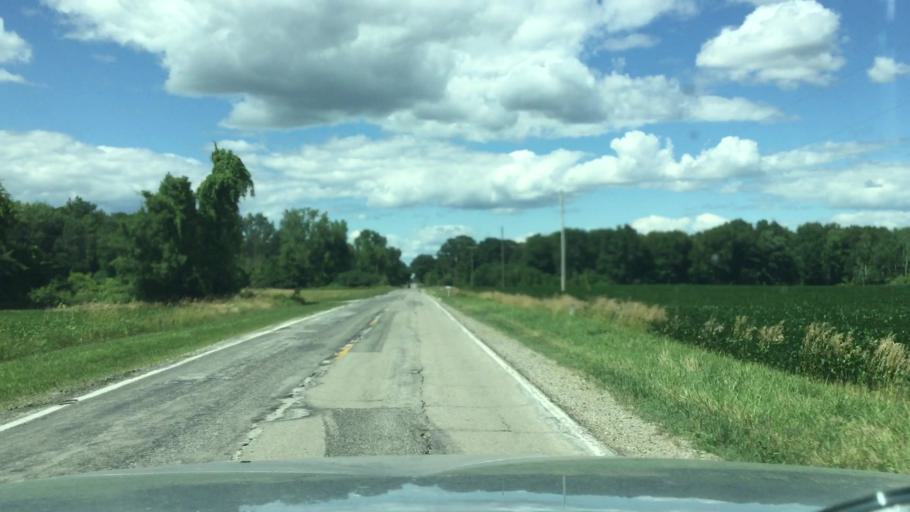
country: US
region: Michigan
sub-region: Saginaw County
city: Hemlock
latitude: 43.3666
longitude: -84.1903
